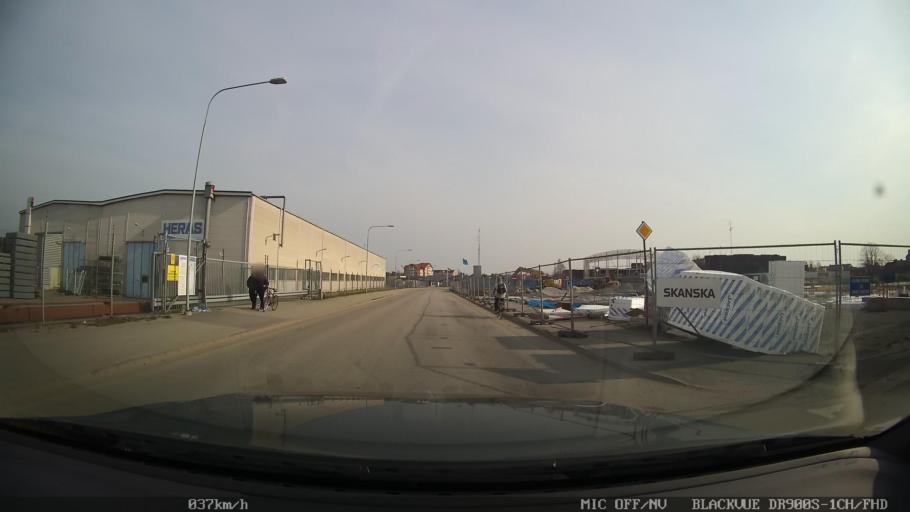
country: SE
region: Skane
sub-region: Ystads Kommun
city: Ystad
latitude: 55.4363
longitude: 13.8327
